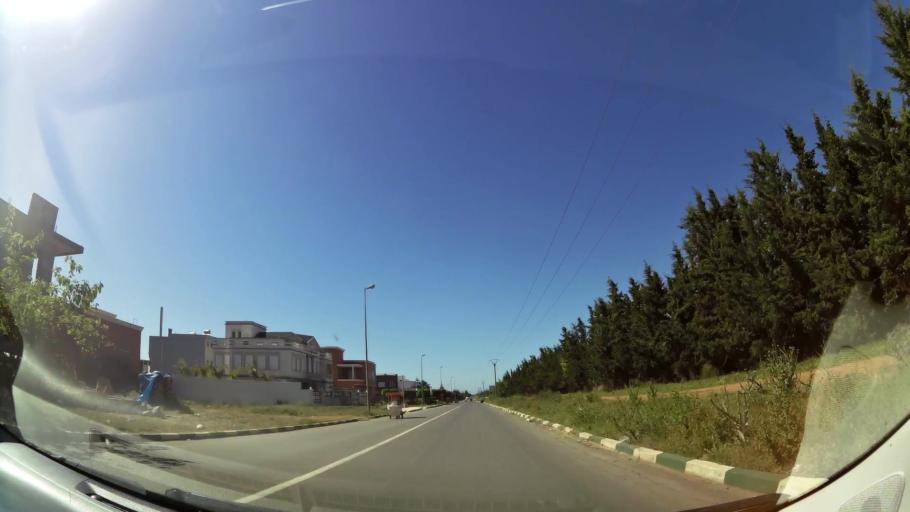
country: MA
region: Oriental
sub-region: Berkane-Taourirt
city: Berkane
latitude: 34.9452
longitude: -2.3265
